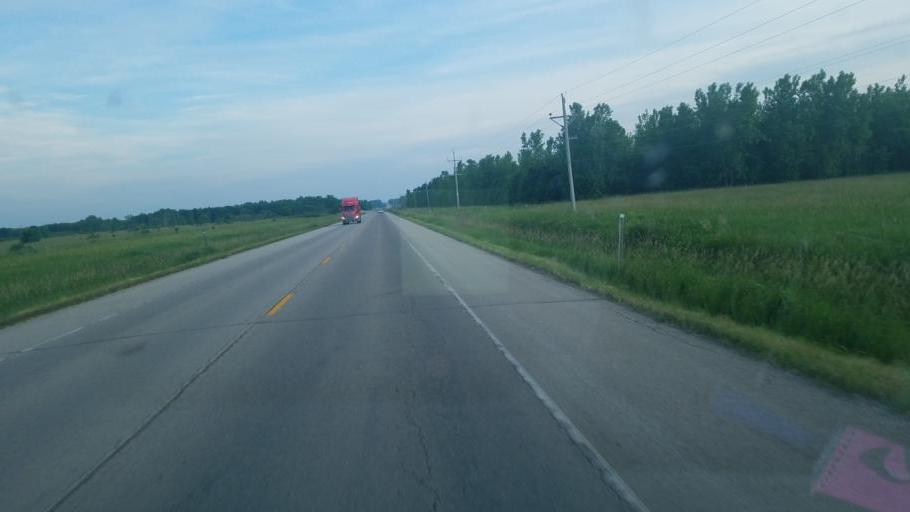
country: US
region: Iowa
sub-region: Benton County
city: Belle Plaine
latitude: 41.8750
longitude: -92.2780
